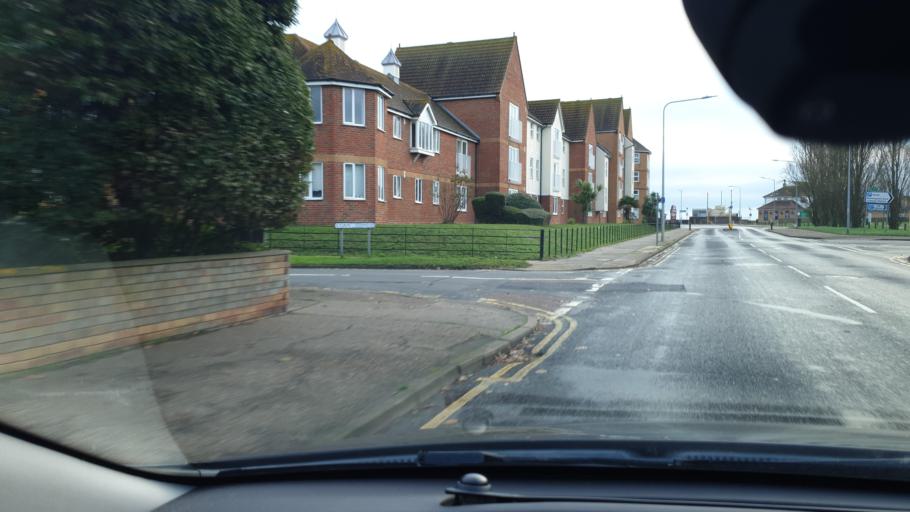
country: GB
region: England
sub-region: Essex
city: Clacton-on-Sea
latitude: 51.7829
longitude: 1.1411
